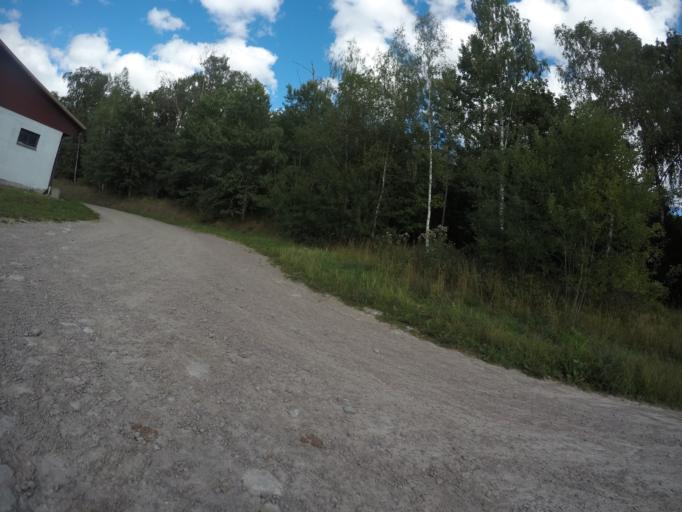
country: SE
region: Vaestmanland
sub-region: Hallstahammars Kommun
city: Kolback
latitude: 59.5191
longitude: 16.2165
